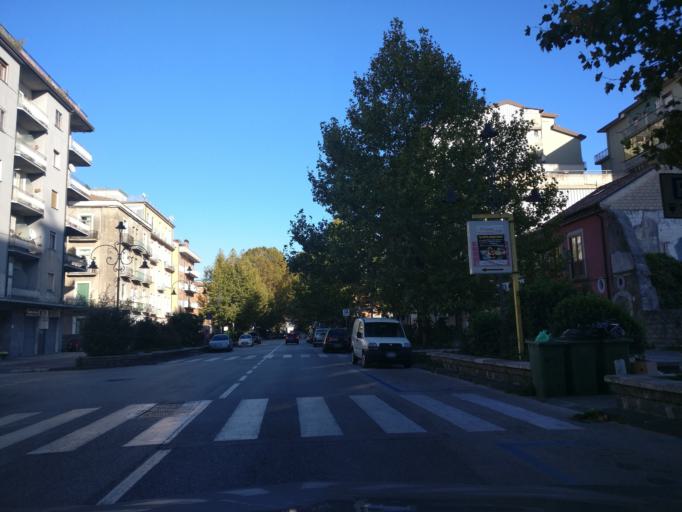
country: IT
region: Campania
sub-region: Provincia di Avellino
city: Avellino
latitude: 40.9127
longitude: 14.7792
